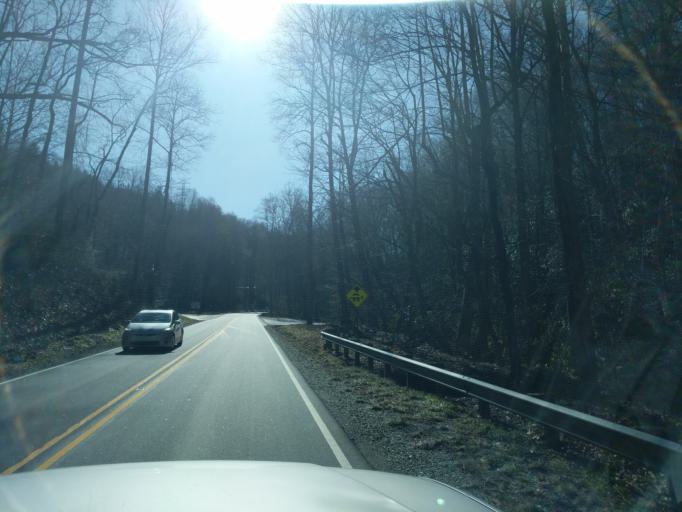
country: US
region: North Carolina
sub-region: Graham County
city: Robbinsville
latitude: 35.2668
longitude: -83.6882
